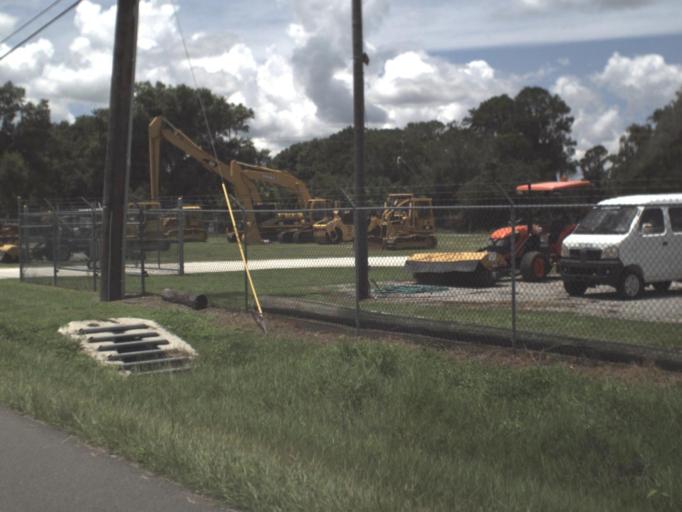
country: US
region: Florida
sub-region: Hillsborough County
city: Plant City
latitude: 28.0204
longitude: -82.0958
